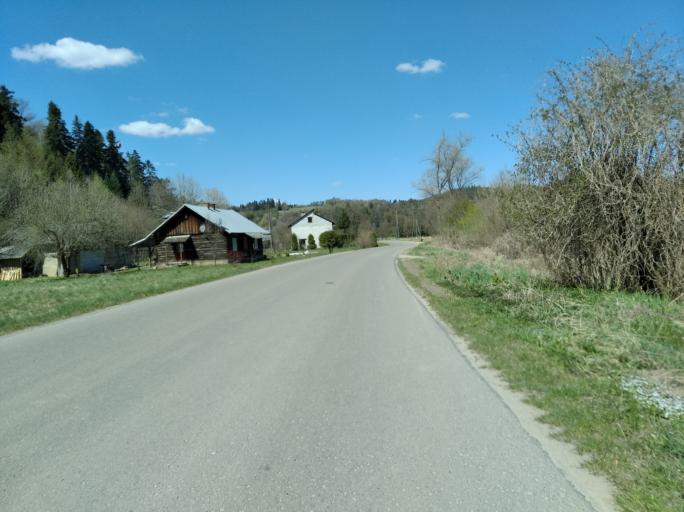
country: PL
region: Subcarpathian Voivodeship
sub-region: Powiat brzozowski
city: Dydnia
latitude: 49.6951
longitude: 22.2004
